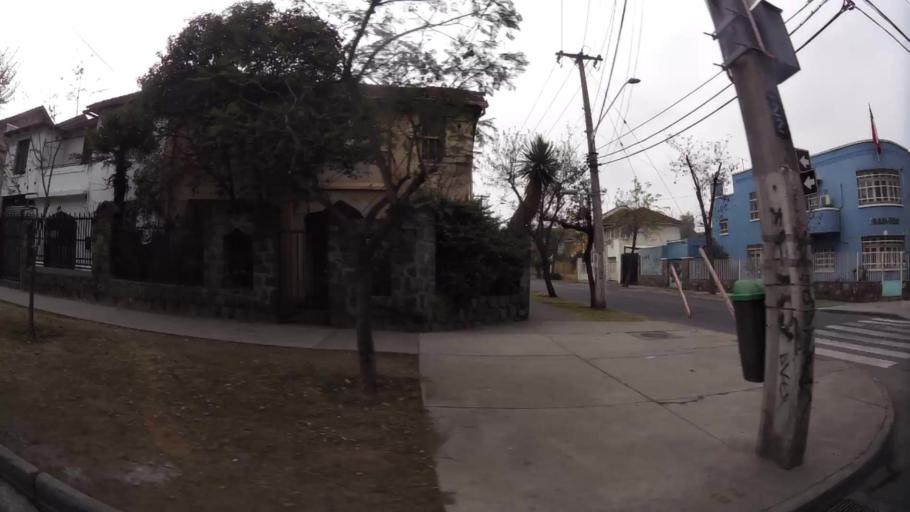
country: CL
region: Santiago Metropolitan
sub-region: Provincia de Santiago
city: Santiago
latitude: -33.4626
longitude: -70.6563
